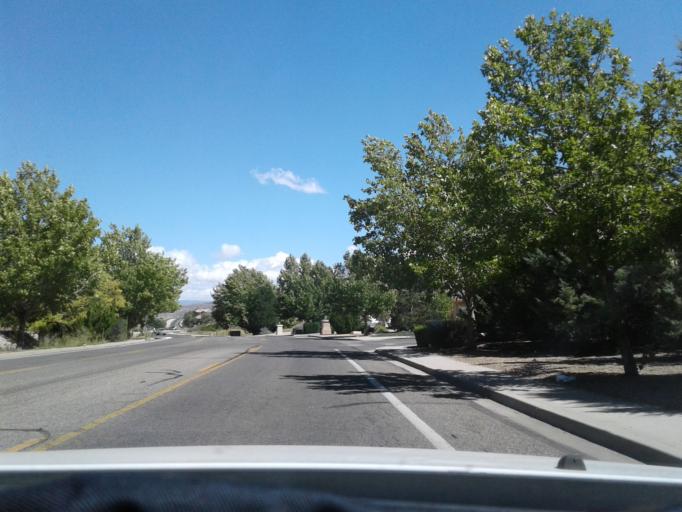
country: US
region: Arizona
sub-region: Yavapai County
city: Prescott
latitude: 34.5706
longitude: -112.4557
